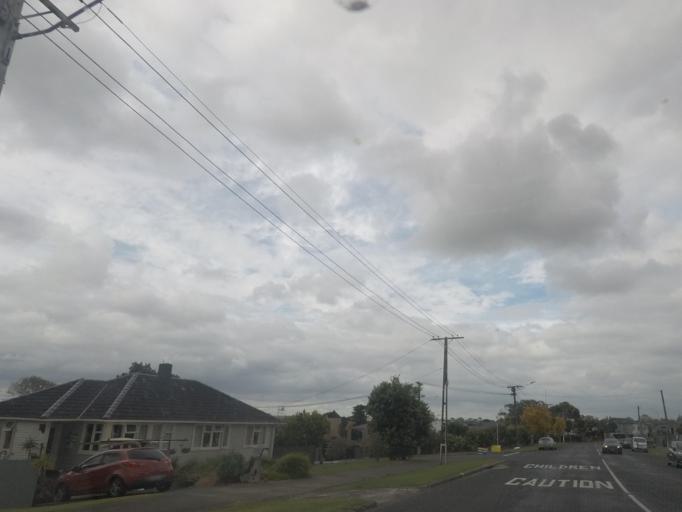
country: NZ
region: Auckland
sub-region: Auckland
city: Tamaki
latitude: -36.8747
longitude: 174.8737
